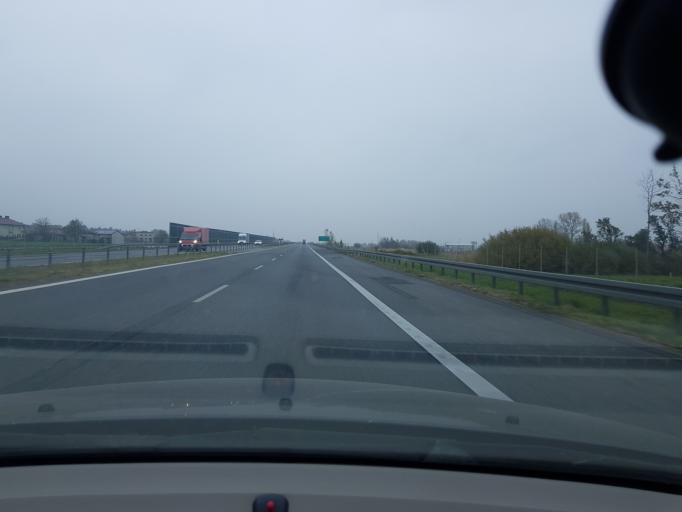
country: PL
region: Masovian Voivodeship
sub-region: Powiat zyrardowski
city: Mszczonow
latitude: 51.9607
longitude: 20.4989
